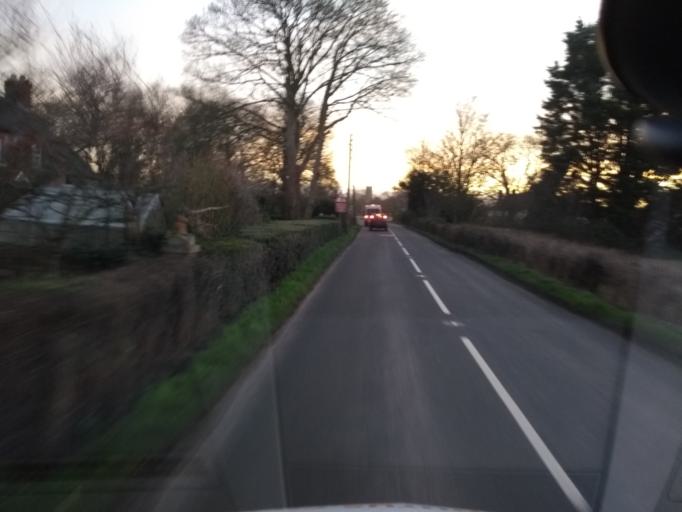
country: GB
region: England
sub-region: Somerset
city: Woolavington
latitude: 51.2258
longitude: -2.8960
